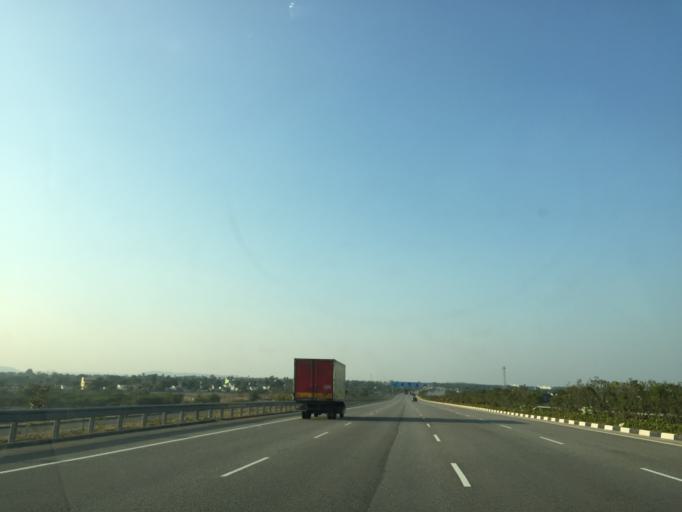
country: IN
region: Telangana
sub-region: Rangareddi
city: Ghatkesar
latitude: 17.4928
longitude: 78.6618
